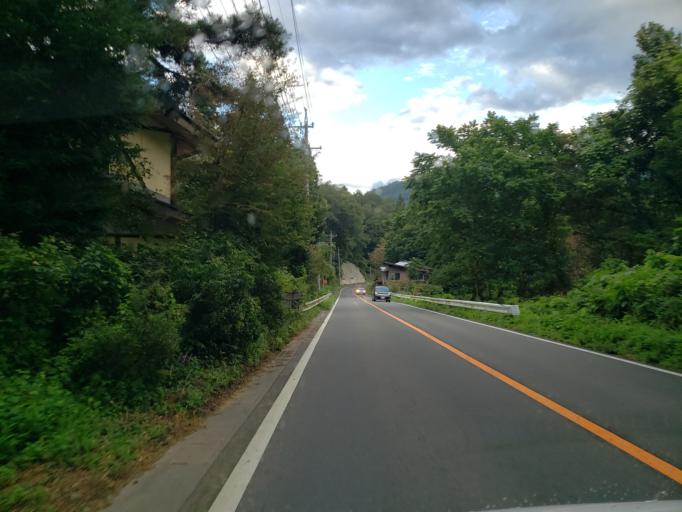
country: JP
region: Nagano
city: Nagano-shi
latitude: 36.6108
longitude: 138.0633
